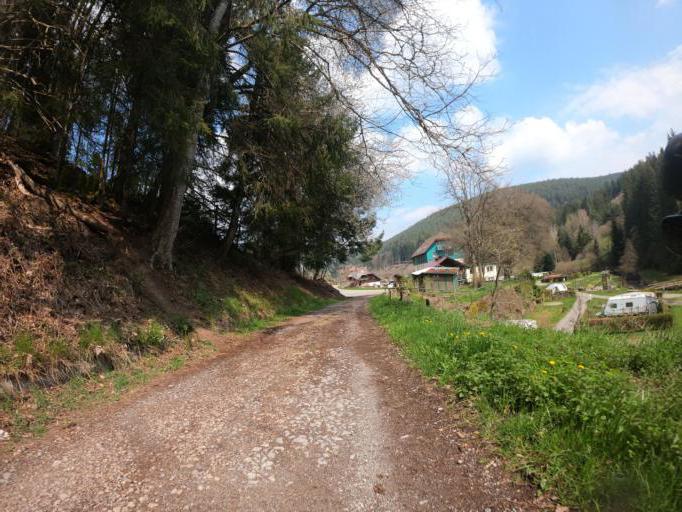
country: DE
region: Baden-Wuerttemberg
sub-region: Karlsruhe Region
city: Bad Wildbad
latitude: 48.7353
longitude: 8.5731
